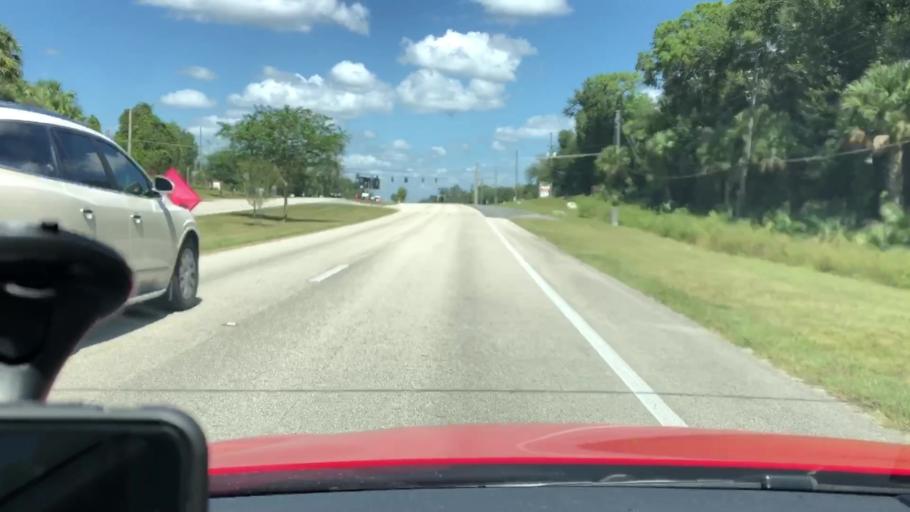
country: US
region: Florida
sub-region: Volusia County
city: Orange City
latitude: 28.9614
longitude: -81.2986
